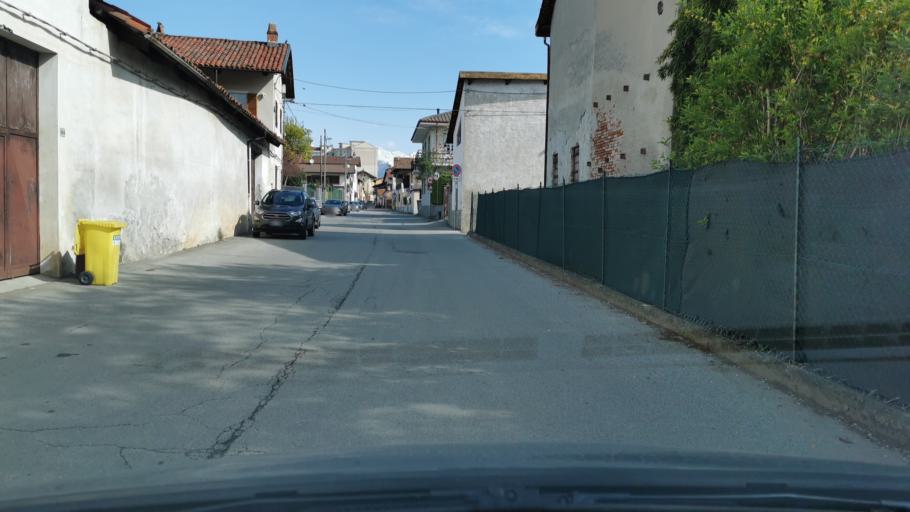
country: IT
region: Piedmont
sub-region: Provincia di Torino
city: Favria
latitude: 45.3278
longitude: 7.6915
